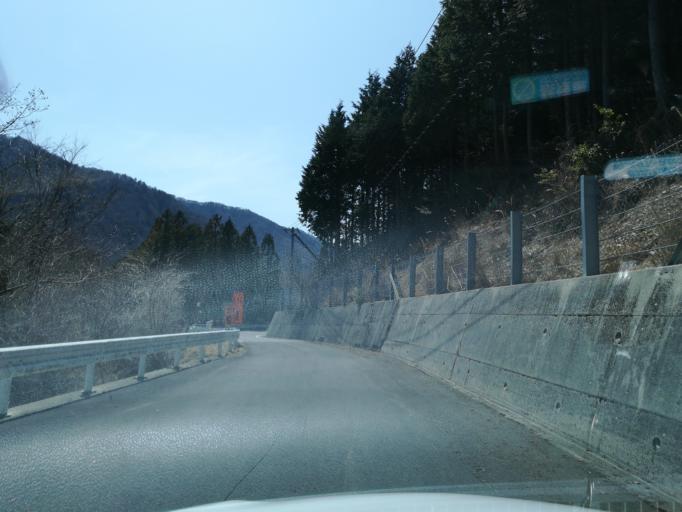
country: JP
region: Tokushima
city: Wakimachi
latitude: 33.8662
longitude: 134.0739
